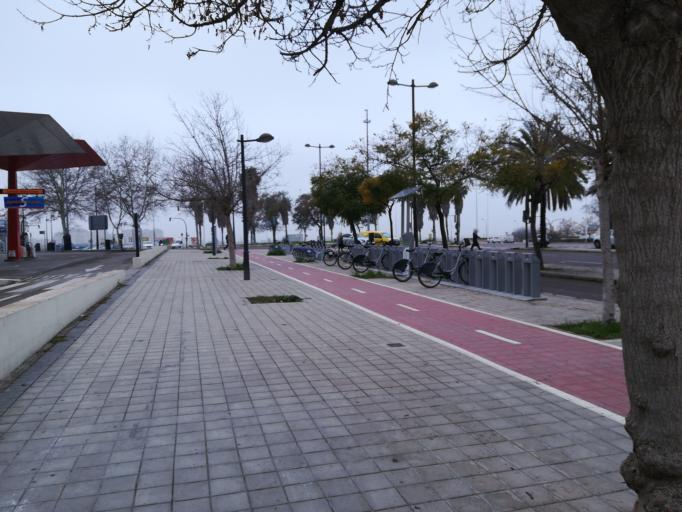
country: ES
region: Valencia
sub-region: Provincia de Valencia
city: Mislata
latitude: 39.4880
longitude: -0.4038
